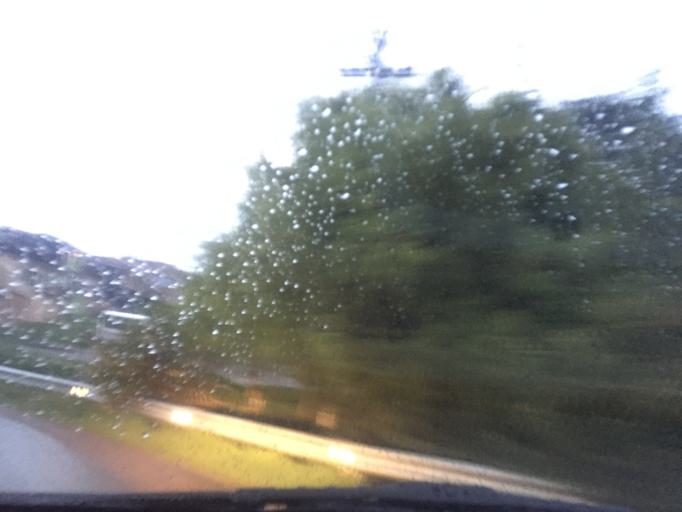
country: CO
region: Cundinamarca
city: Cogua
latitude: 5.0667
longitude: -73.9774
